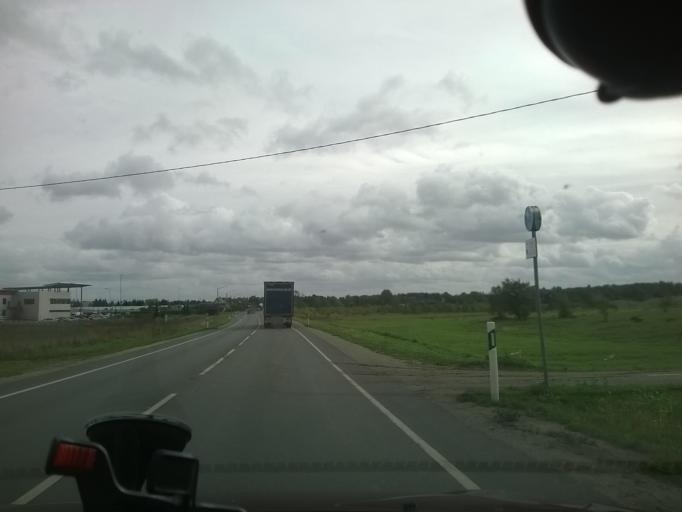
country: EE
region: Harju
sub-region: Rae vald
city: Jueri
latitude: 59.3810
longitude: 24.8337
